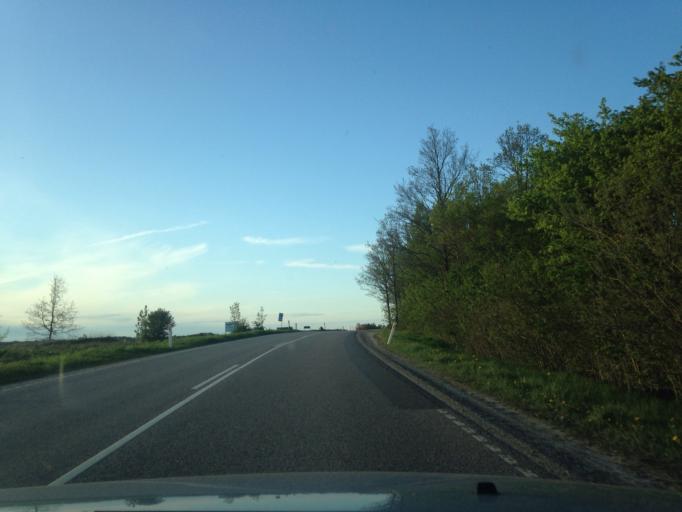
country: DK
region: Zealand
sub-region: Greve Kommune
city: Tune
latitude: 55.6215
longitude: 12.1846
